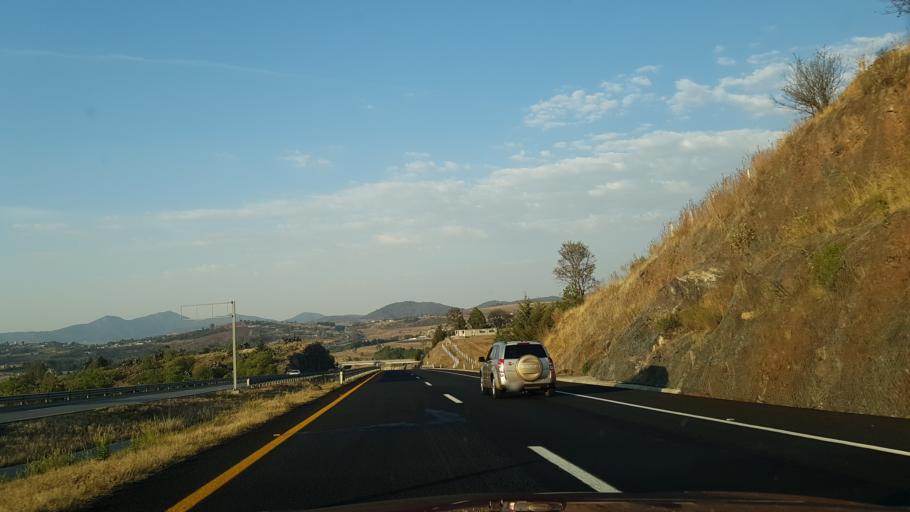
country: MX
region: Mexico
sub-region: Atlacomulco
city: La Mesa de Chosto
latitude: 19.8533
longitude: -99.8830
